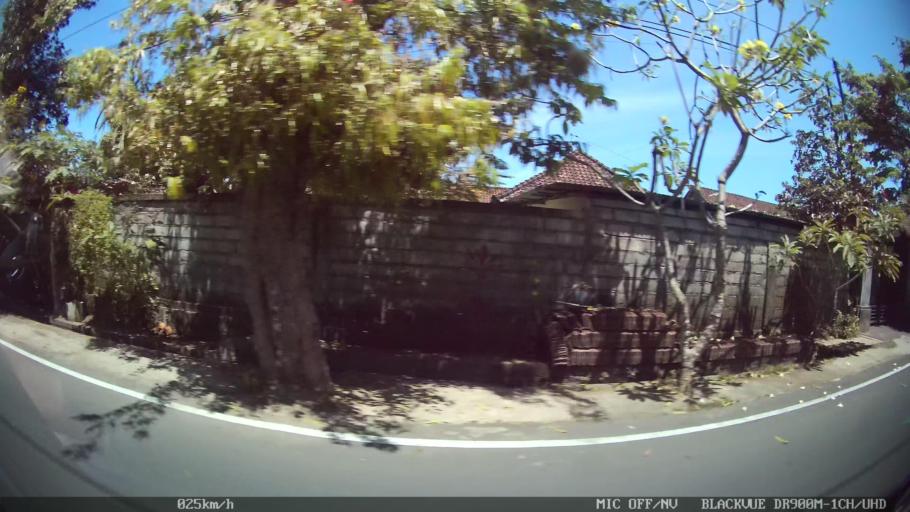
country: ID
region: Bali
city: Klungkung
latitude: -8.5708
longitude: 115.3347
